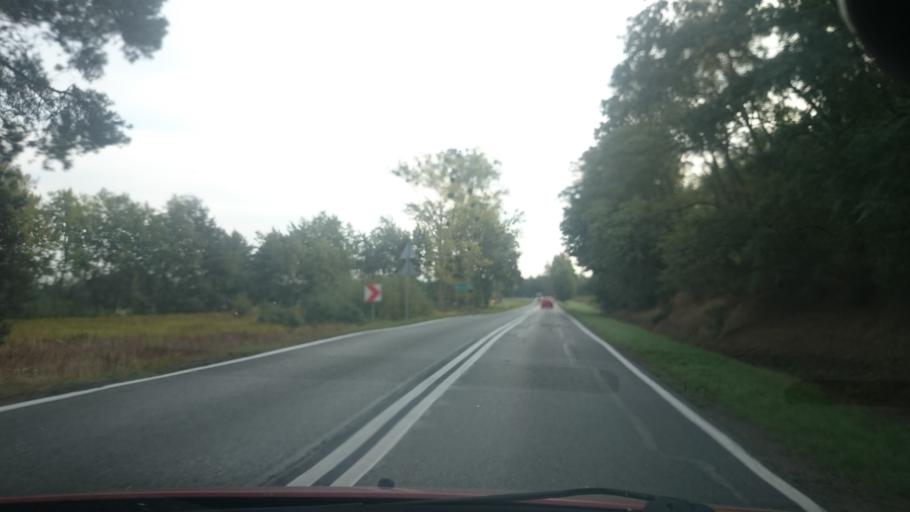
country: PL
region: Lower Silesian Voivodeship
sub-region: Powiat trzebnicki
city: Trzebnica
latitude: 51.3700
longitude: 17.1610
